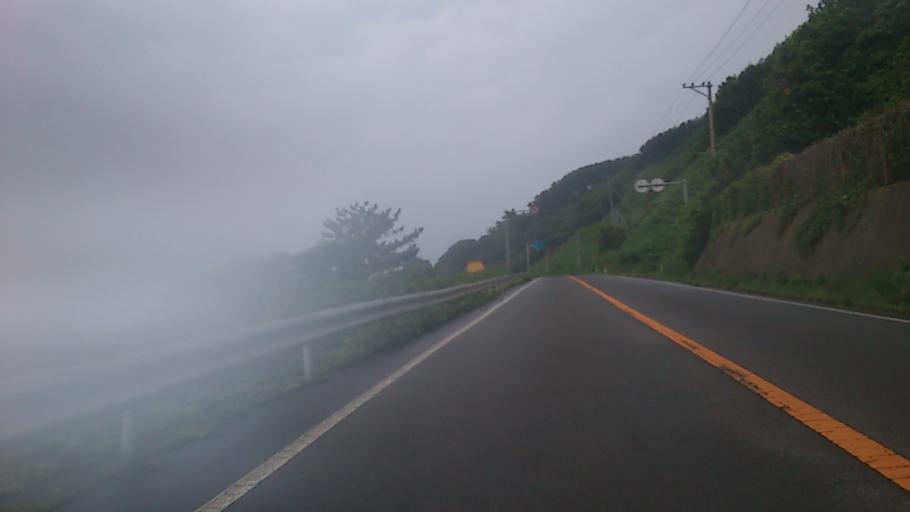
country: JP
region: Akita
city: Noshiromachi
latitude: 40.4408
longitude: 139.9402
